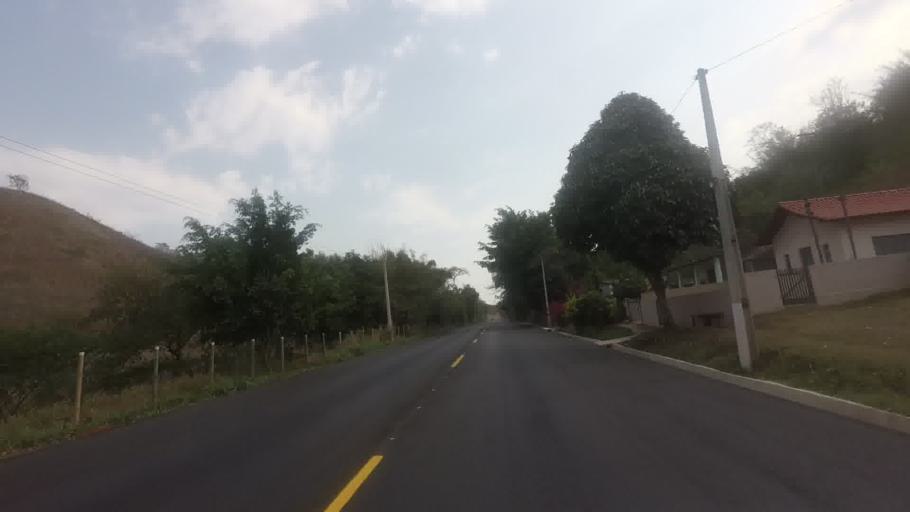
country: BR
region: Rio de Janeiro
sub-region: Bom Jesus Do Itabapoana
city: Bom Jesus do Itabapoana
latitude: -21.2367
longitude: -41.7510
